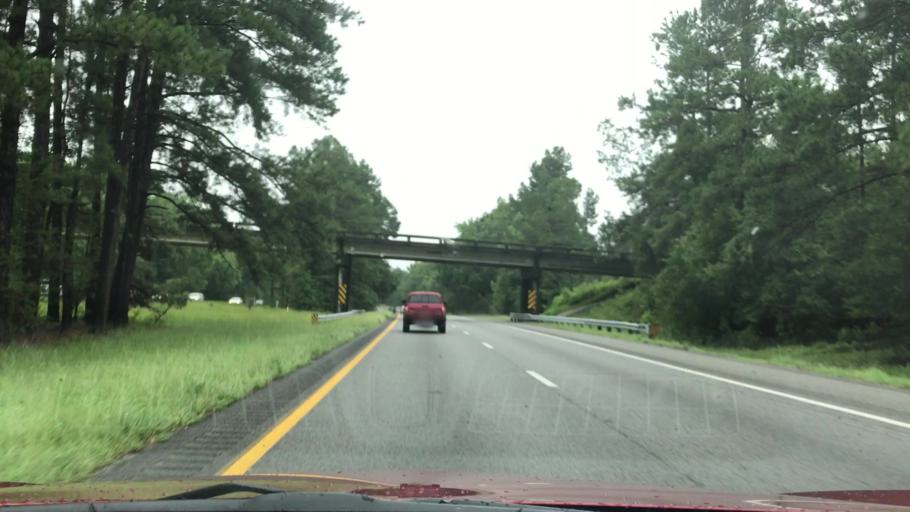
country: US
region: South Carolina
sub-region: Dorchester County
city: Ridgeville
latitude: 33.1593
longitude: -80.3529
